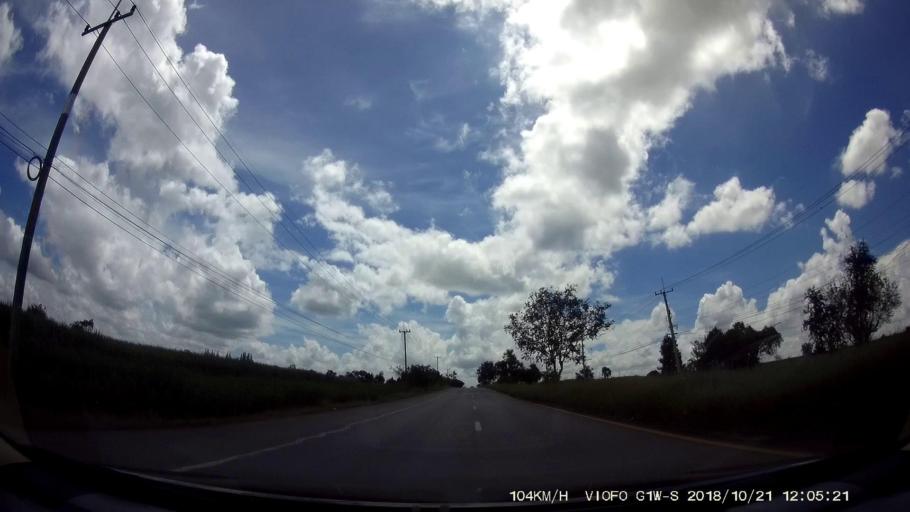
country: TH
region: Chaiyaphum
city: Chatturat
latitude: 15.4802
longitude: 101.8234
